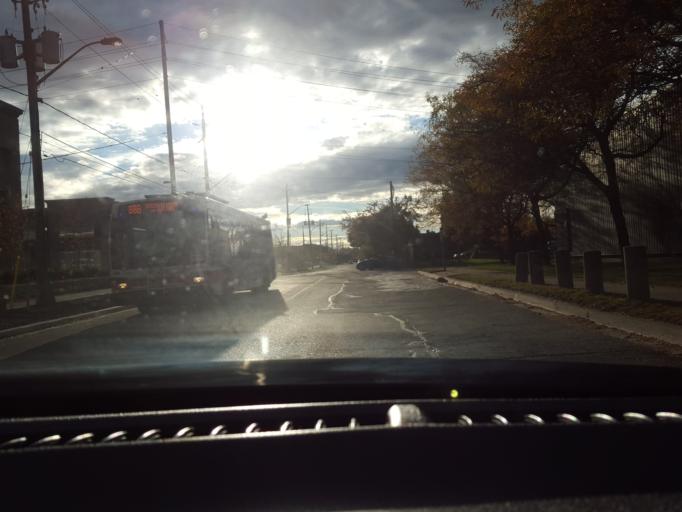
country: CA
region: Ontario
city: Toronto
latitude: 43.7130
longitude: -79.3499
